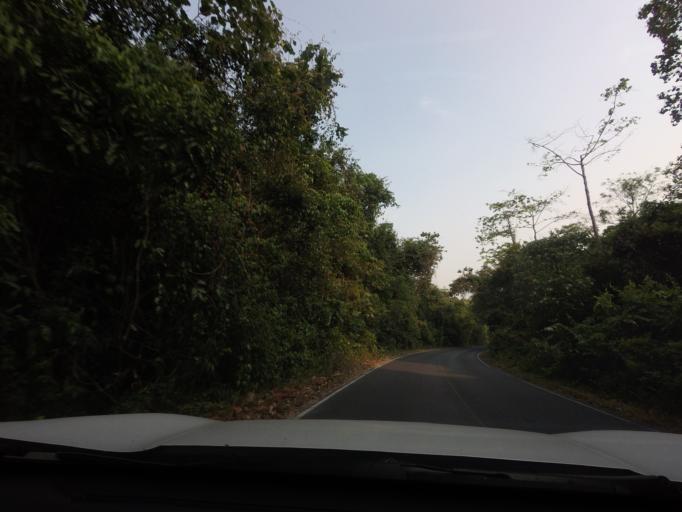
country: TH
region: Nakhon Nayok
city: Nakhon Nayok
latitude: 14.3400
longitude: 101.3505
